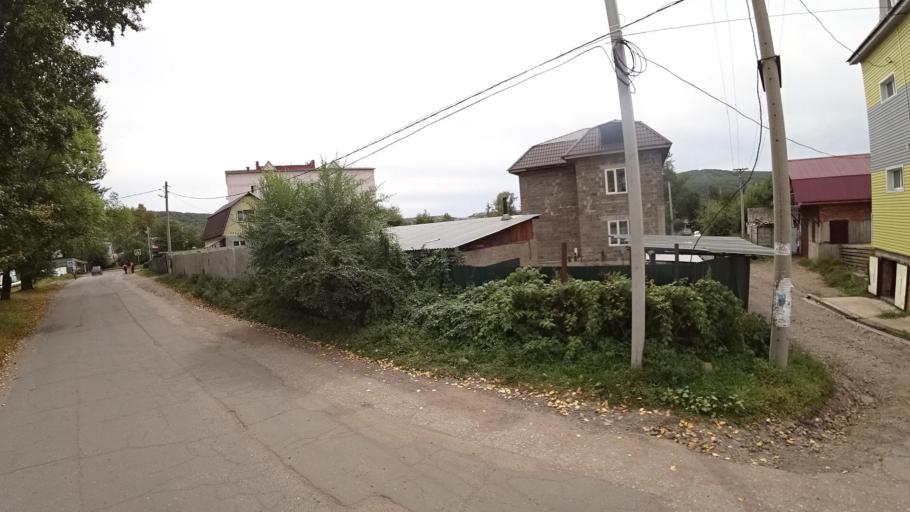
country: RU
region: Jewish Autonomous Oblast
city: Khingansk
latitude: 49.0154
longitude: 131.0553
